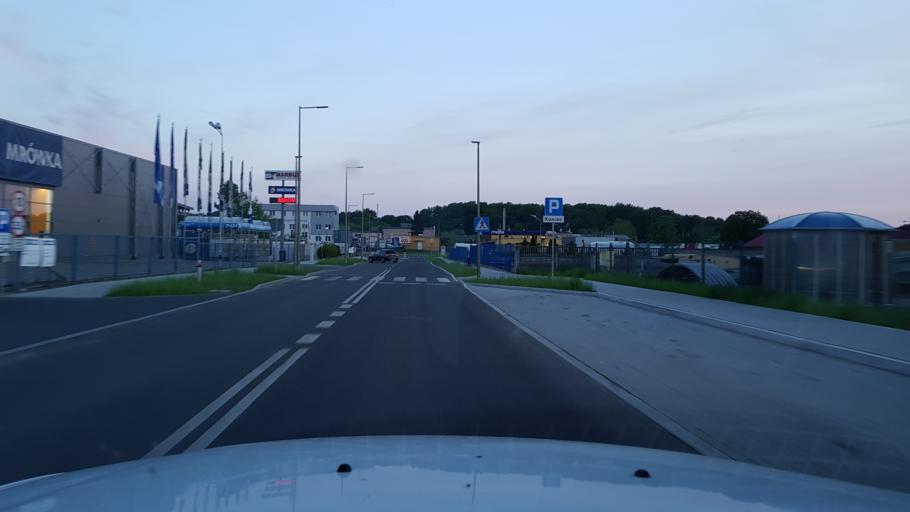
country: PL
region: West Pomeranian Voivodeship
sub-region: Powiat goleniowski
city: Goleniow
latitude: 53.5597
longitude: 14.8459
